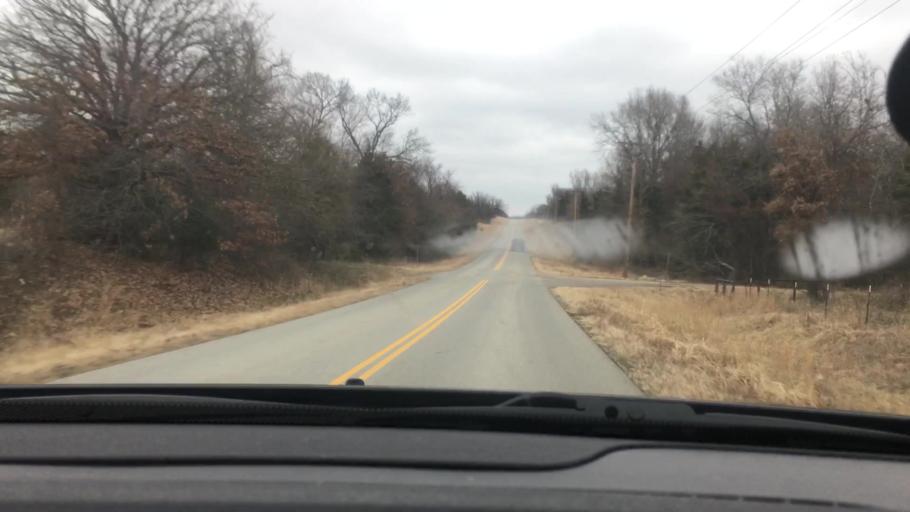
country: US
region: Oklahoma
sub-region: Atoka County
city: Atoka
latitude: 34.3305
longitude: -96.0754
